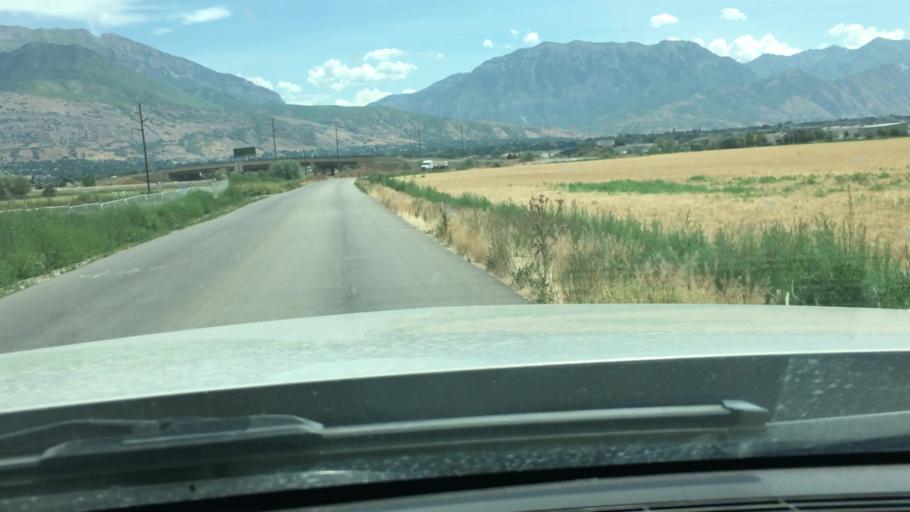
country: US
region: Utah
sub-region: Utah County
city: Pleasant Grove
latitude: 40.3432
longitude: -111.7624
